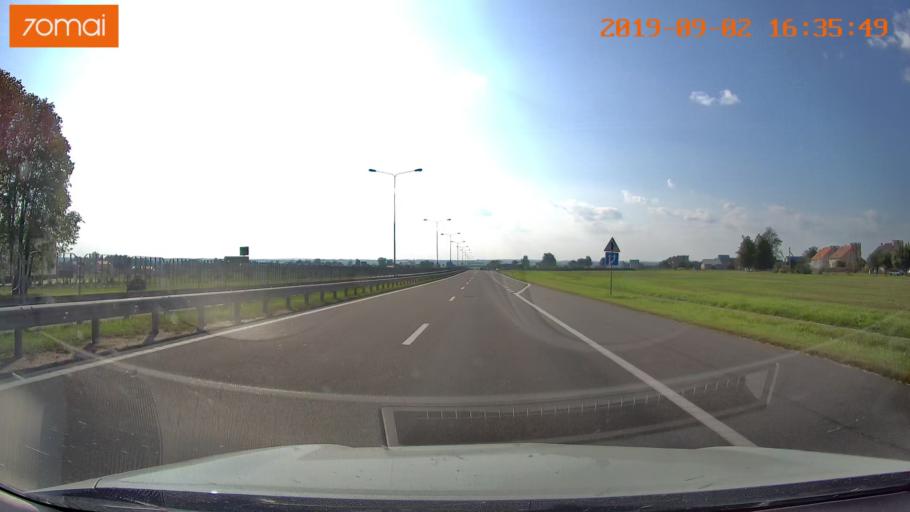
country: BY
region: Minsk
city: Smilavichy
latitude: 53.7598
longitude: 27.9940
